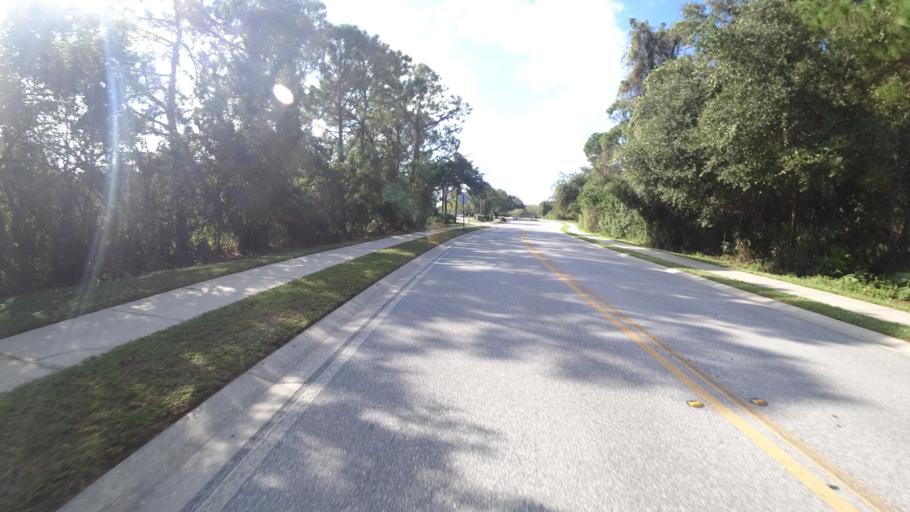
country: US
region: Florida
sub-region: Sarasota County
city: The Meadows
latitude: 27.3954
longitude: -82.4524
